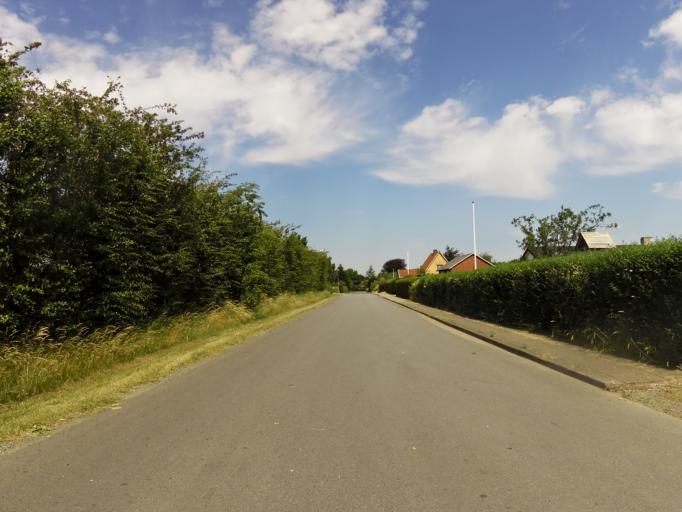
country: DK
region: South Denmark
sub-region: Haderslev Kommune
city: Vojens
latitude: 55.1965
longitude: 9.2114
